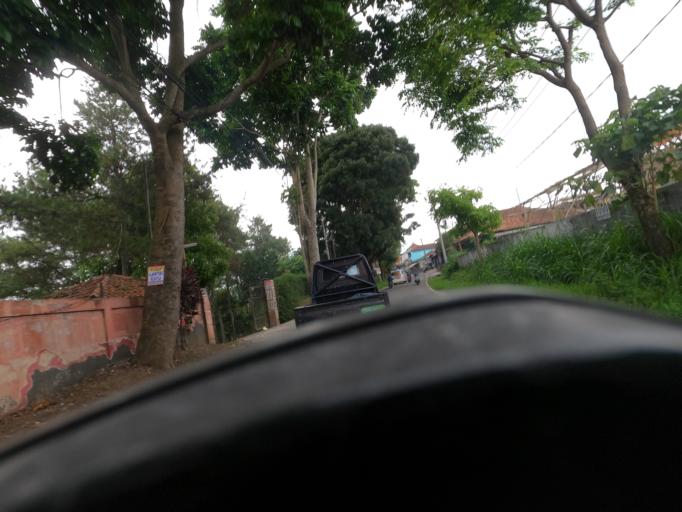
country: ID
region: West Java
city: Lembang
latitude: -6.8183
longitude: 107.6031
